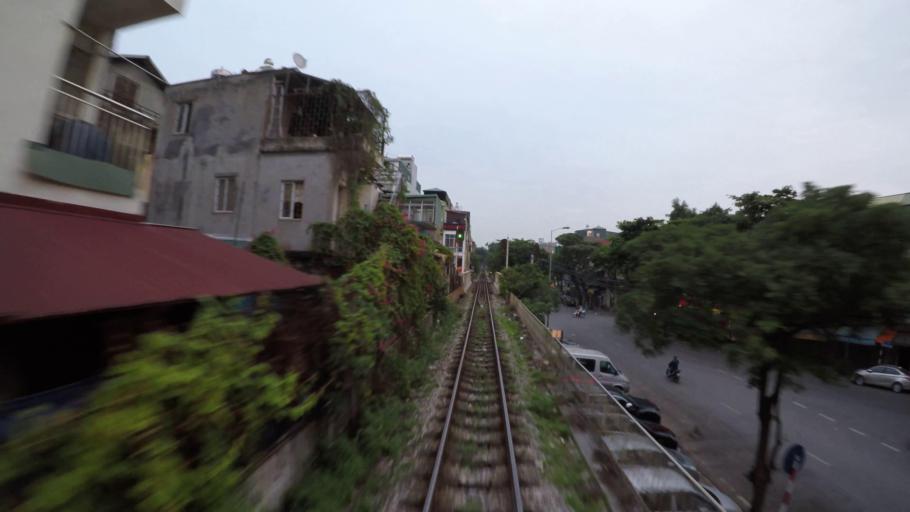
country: VN
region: Ha Noi
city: Hoan Kiem
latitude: 21.0419
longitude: 105.8549
